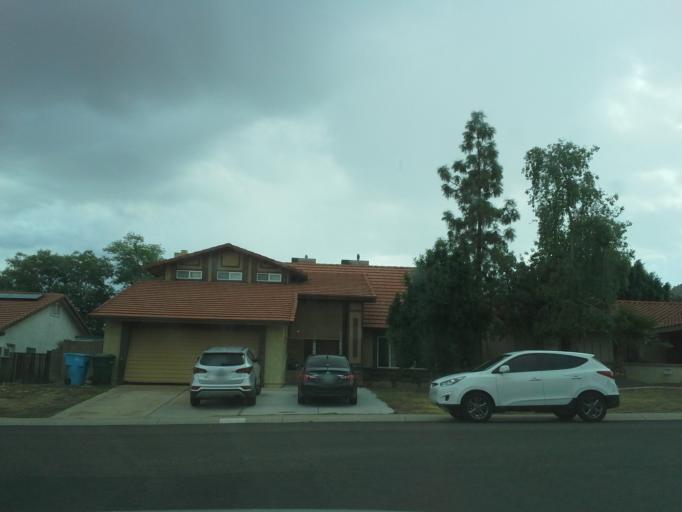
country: US
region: Arizona
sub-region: Maricopa County
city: Paradise Valley
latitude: 33.6174
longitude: -112.0358
